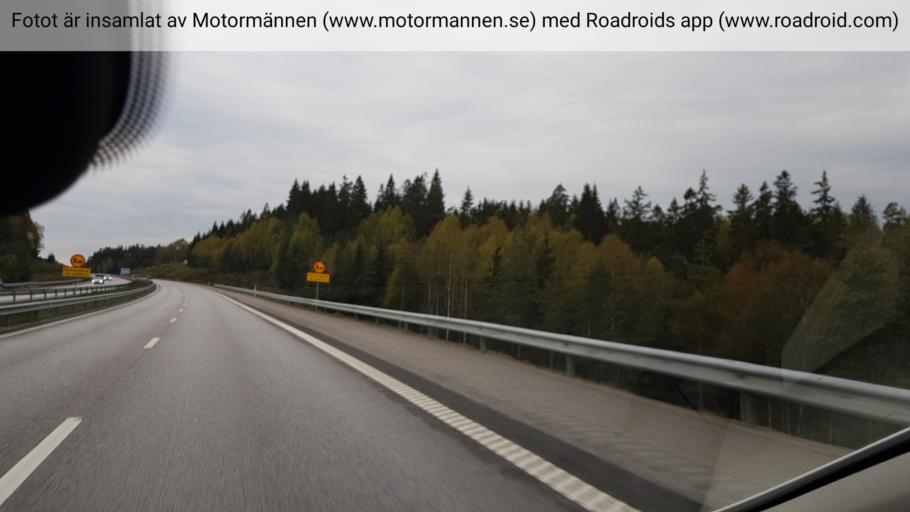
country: SE
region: Vaestra Goetaland
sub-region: Harryda Kommun
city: Hindas
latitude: 57.6748
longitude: 12.4653
